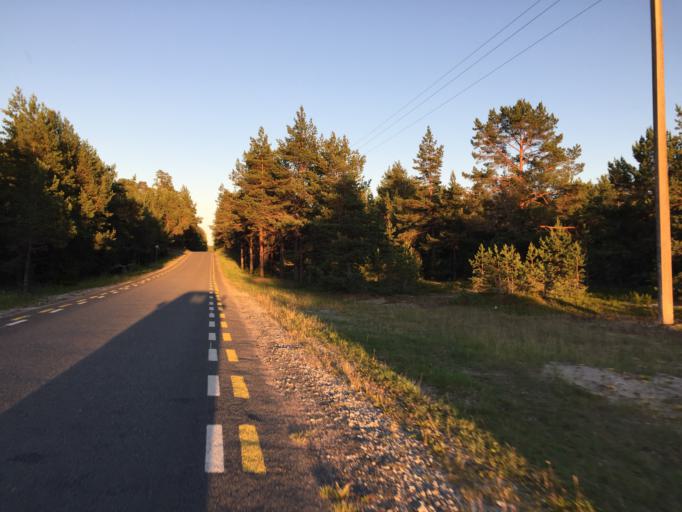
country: EE
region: Harju
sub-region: Raasiku vald
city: Raasiku
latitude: 59.5066
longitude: 25.2803
